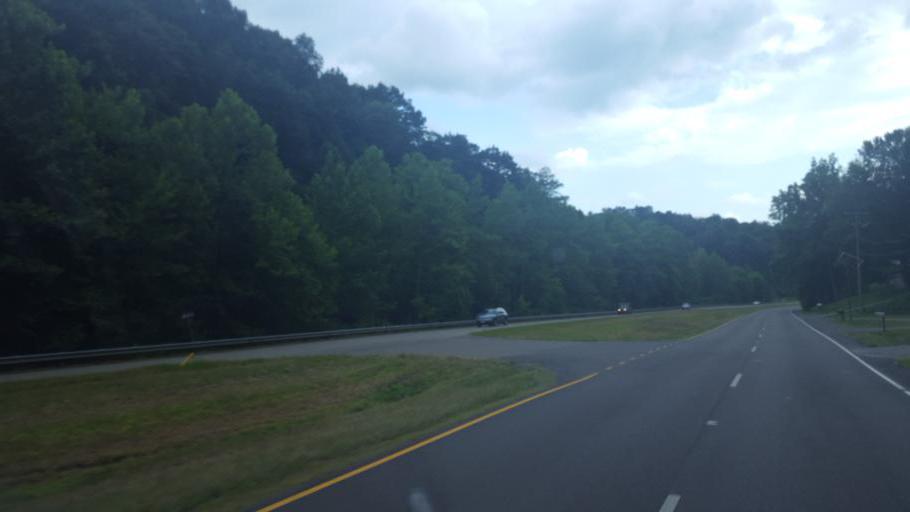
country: US
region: Virginia
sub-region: Wise County
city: Pound
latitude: 37.0763
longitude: -82.5990
